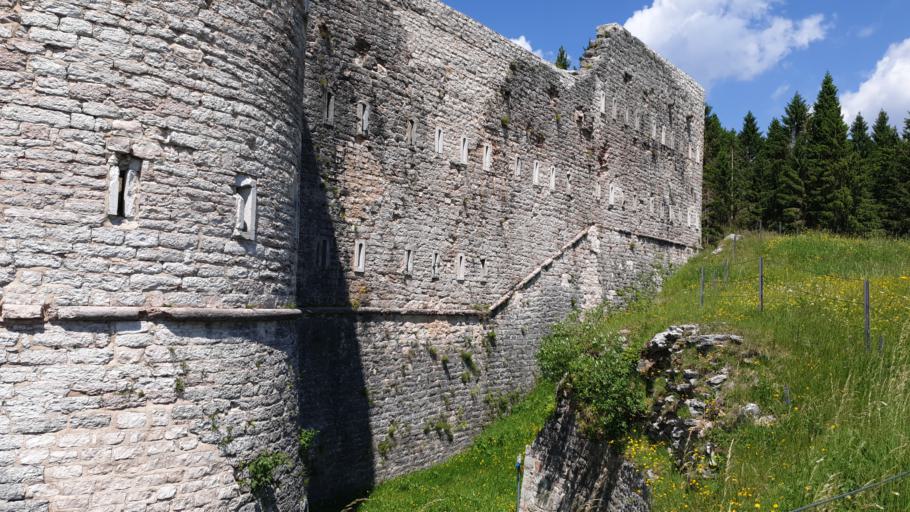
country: IT
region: Veneto
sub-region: Provincia di Vicenza
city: Canove di Roana
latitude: 45.8971
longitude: 11.4812
